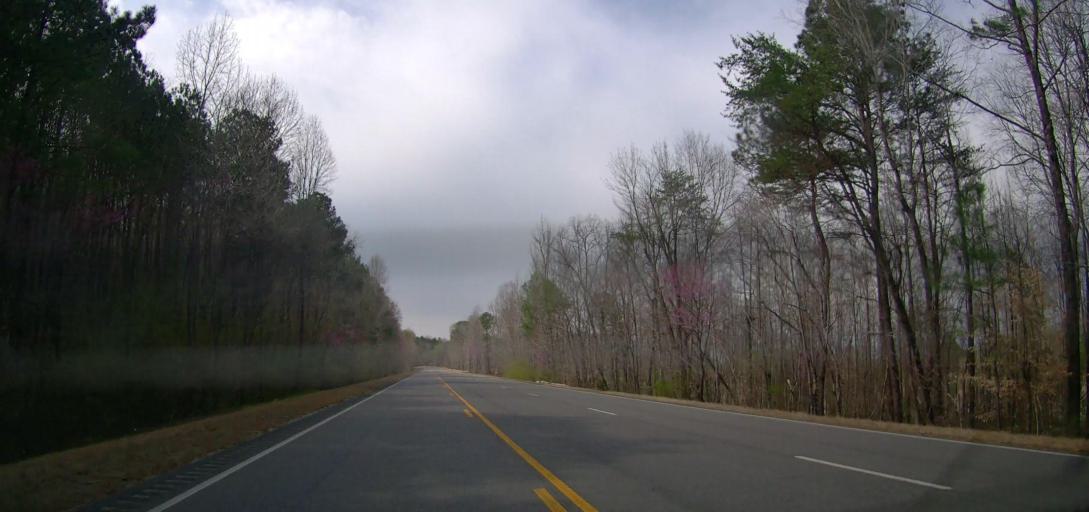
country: US
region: Alabama
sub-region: Walker County
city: Carbon Hill
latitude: 33.9128
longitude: -87.5620
